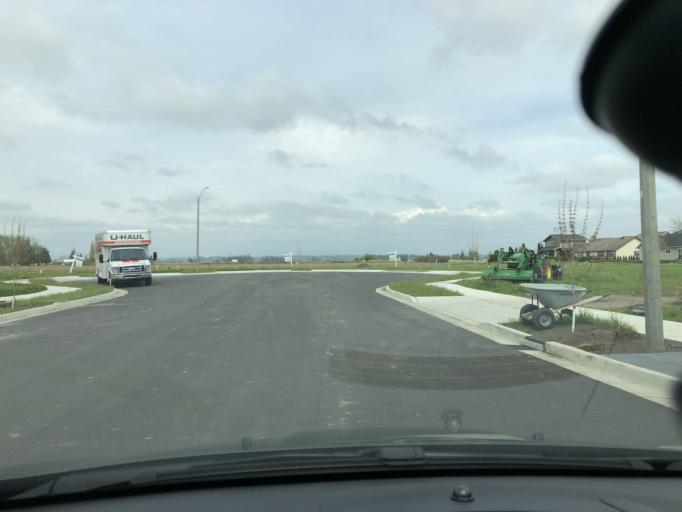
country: US
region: Washington
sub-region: Whatcom County
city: Lynden
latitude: 48.9496
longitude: -122.4698
